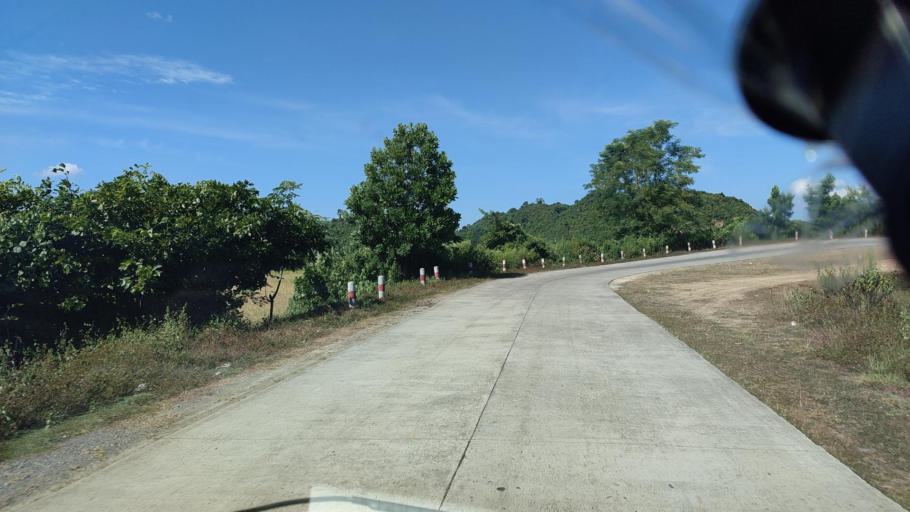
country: MM
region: Rakhine
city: Sittwe
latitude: 20.3185
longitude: 93.3474
